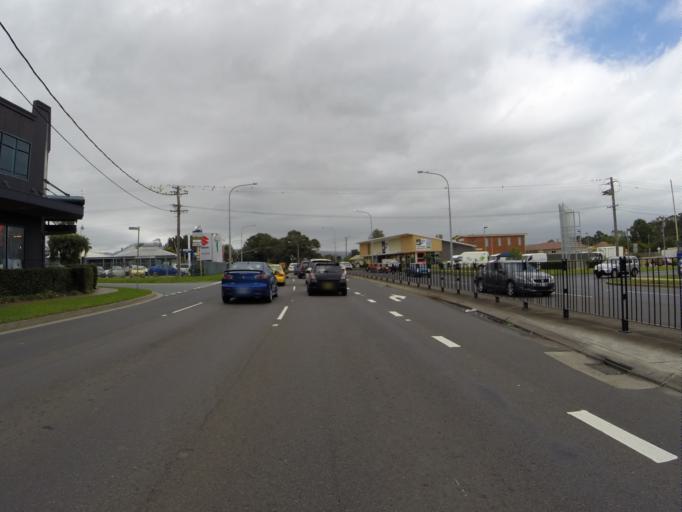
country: AU
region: New South Wales
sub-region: Shoalhaven Shire
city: Nowra
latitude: -34.8734
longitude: 150.6057
